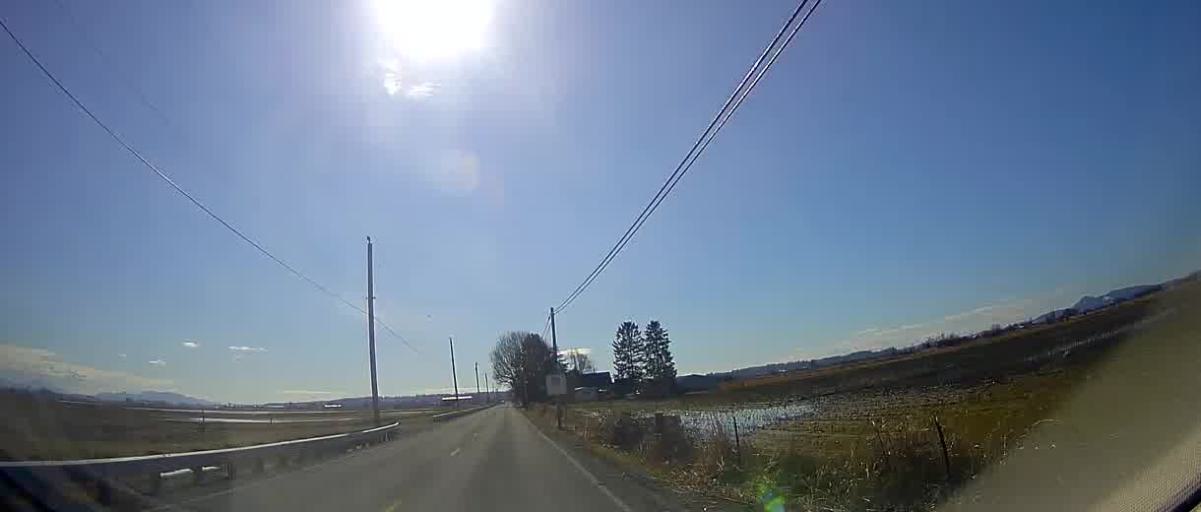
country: US
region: Washington
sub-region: Skagit County
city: Burlington
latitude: 48.5538
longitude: -122.4442
